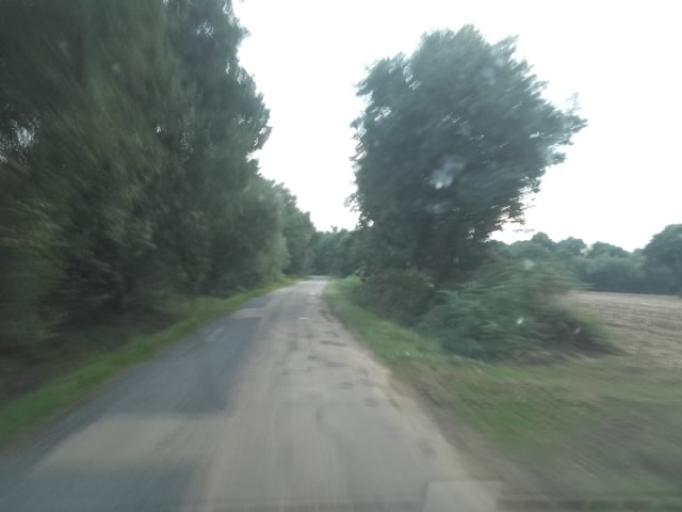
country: FR
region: Brittany
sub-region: Departement des Cotes-d'Armor
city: Lanvollon
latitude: 48.6297
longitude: -2.9662
